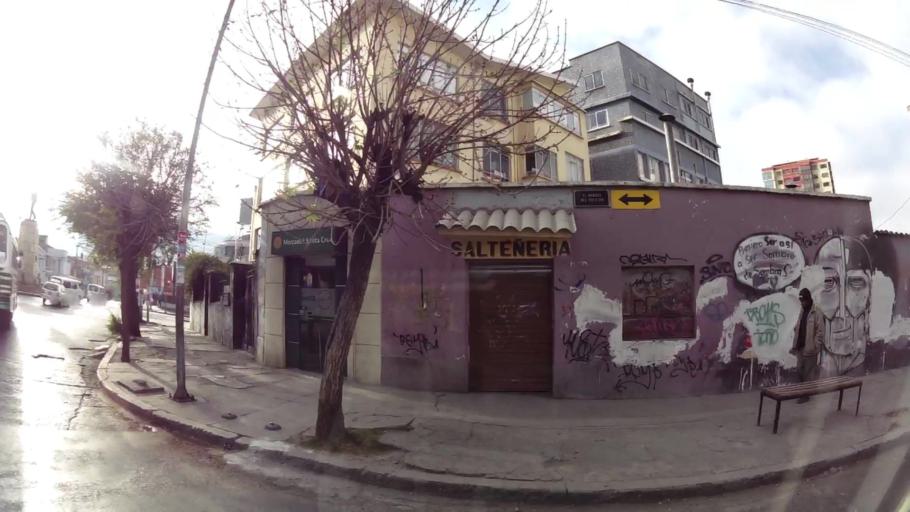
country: BO
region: La Paz
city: La Paz
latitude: -16.4946
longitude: -68.1217
